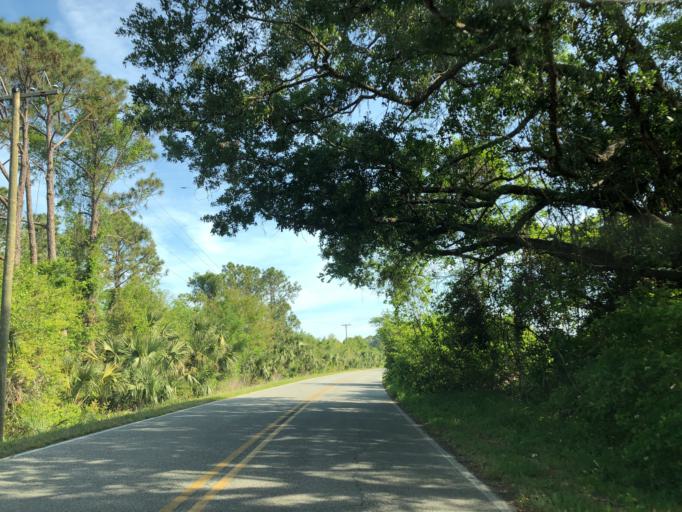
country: US
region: Florida
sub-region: Lake County
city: Astatula
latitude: 28.7142
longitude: -81.6728
